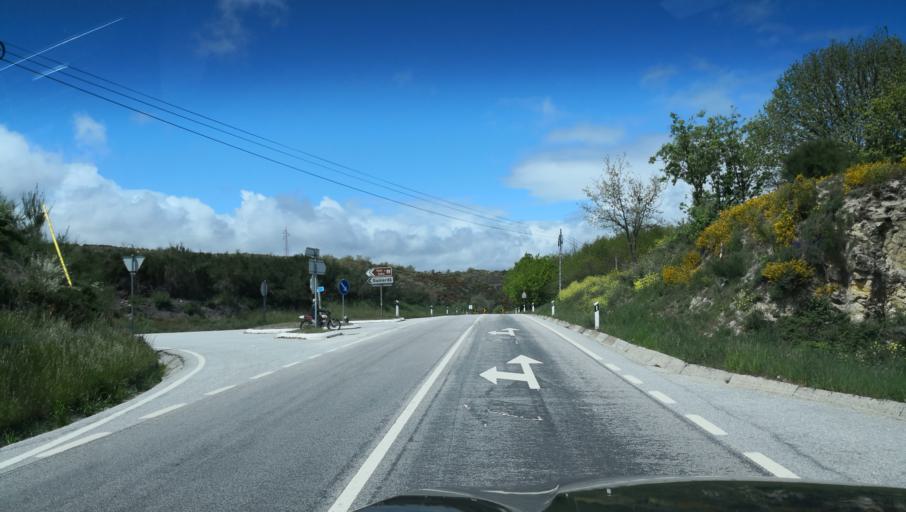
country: PT
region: Vila Real
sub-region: Vila Real
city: Vila Real
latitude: 41.3969
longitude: -7.7012
